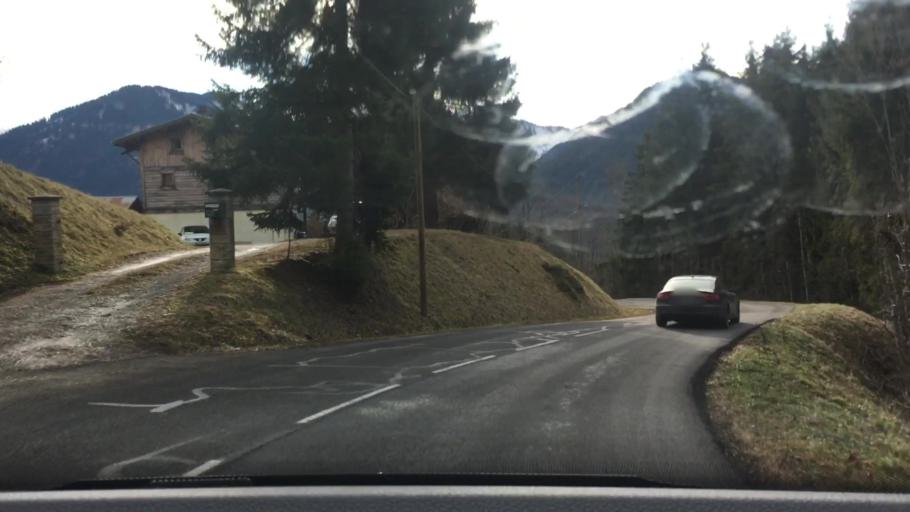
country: FR
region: Rhone-Alpes
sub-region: Departement de la Haute-Savoie
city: Abondance
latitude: 46.2799
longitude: 6.6318
